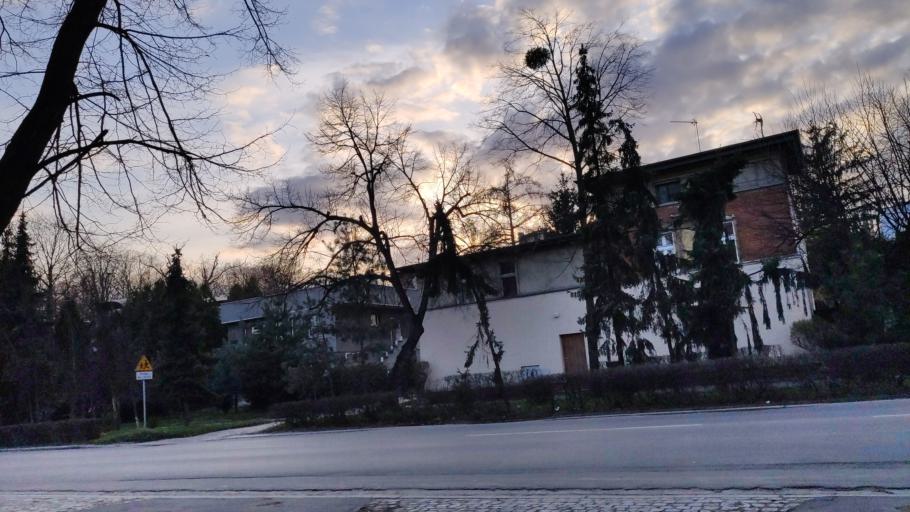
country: PL
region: Lower Silesian Voivodeship
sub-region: Powiat wroclawski
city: Wroclaw
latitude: 51.0785
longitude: 17.0152
